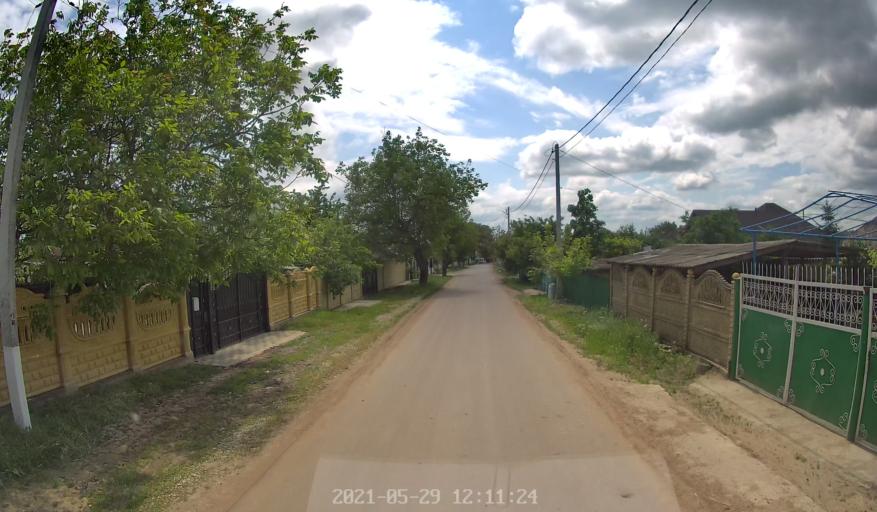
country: MD
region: Hincesti
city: Hincesti
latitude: 46.8831
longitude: 28.6295
